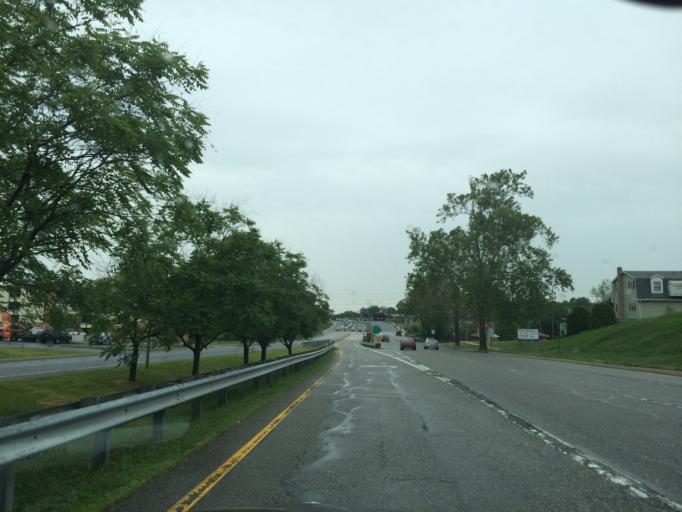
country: US
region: Maryland
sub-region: Washington County
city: Hagerstown
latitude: 39.6294
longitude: -77.7003
